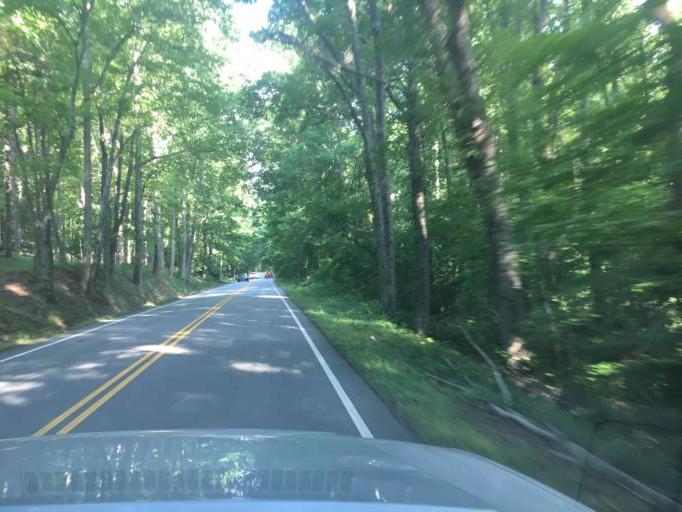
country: US
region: South Carolina
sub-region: Greenville County
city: Simpsonville
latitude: 34.7694
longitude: -82.2630
